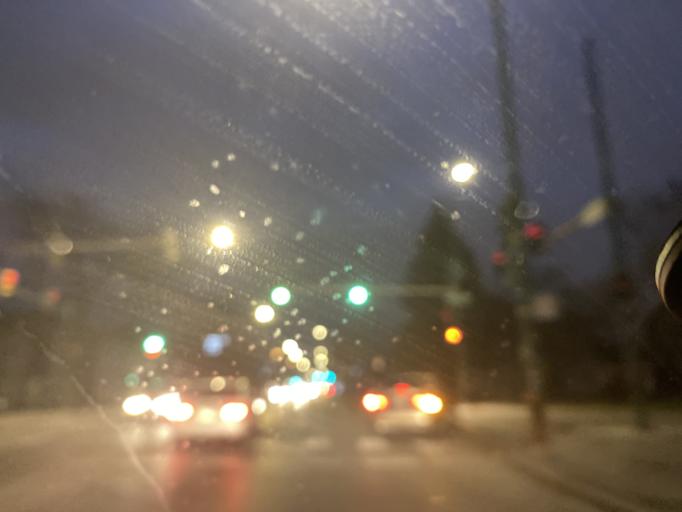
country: US
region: Illinois
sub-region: Cook County
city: Chicago
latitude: 41.7799
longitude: -87.6377
